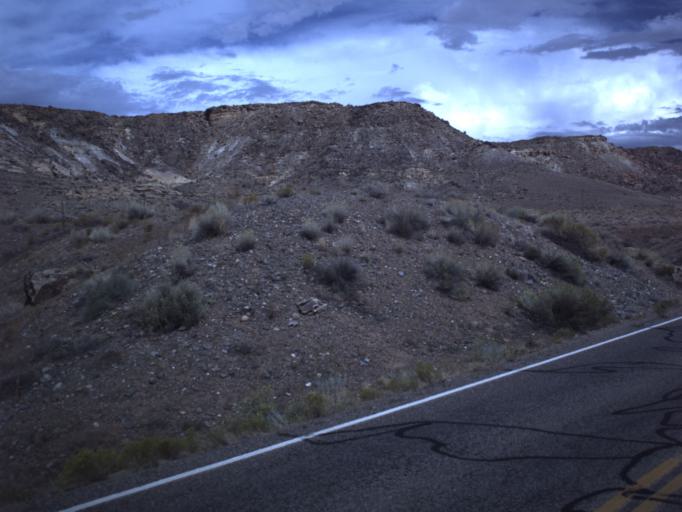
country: US
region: Colorado
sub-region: Montezuma County
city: Towaoc
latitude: 37.2140
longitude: -109.1795
